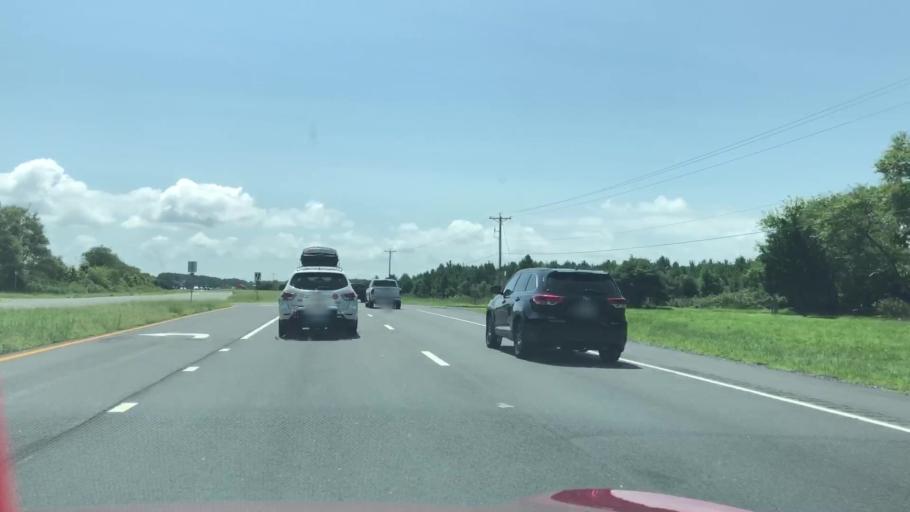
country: US
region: Virginia
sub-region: Northampton County
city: Cape Charles
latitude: 37.1474
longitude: -75.9715
